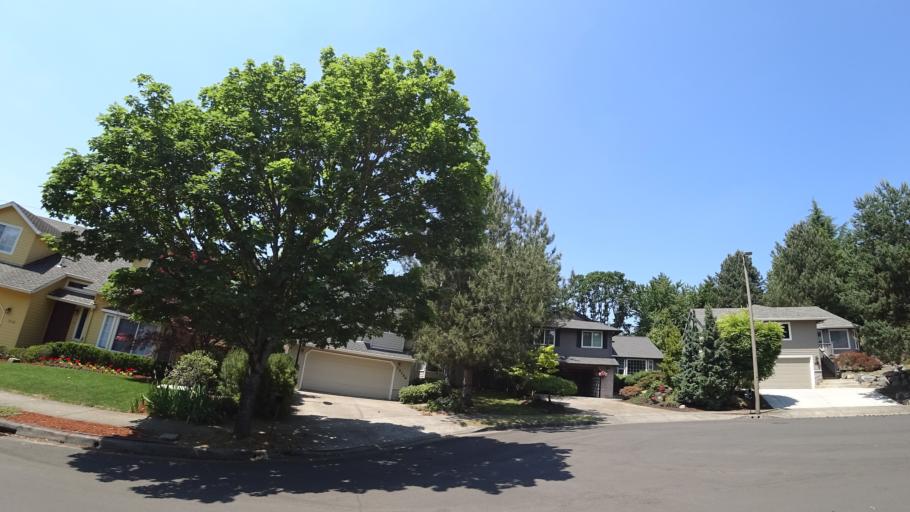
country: US
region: Oregon
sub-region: Washington County
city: Metzger
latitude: 45.4317
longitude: -122.7277
